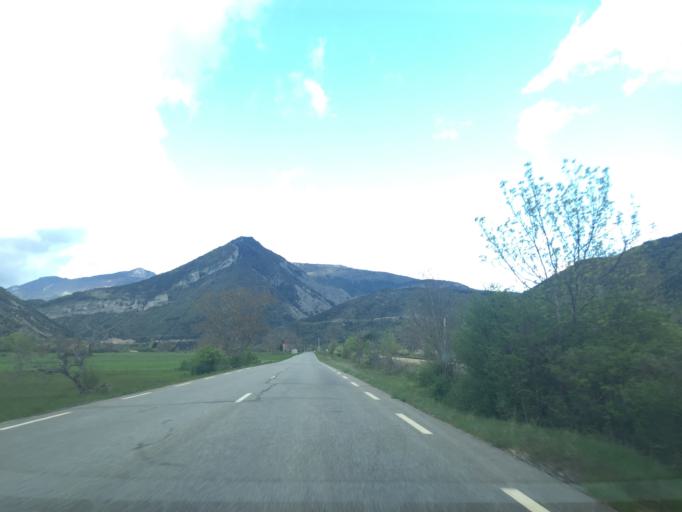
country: FR
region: Provence-Alpes-Cote d'Azur
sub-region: Departement des Hautes-Alpes
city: Veynes
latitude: 44.5298
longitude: 5.7686
